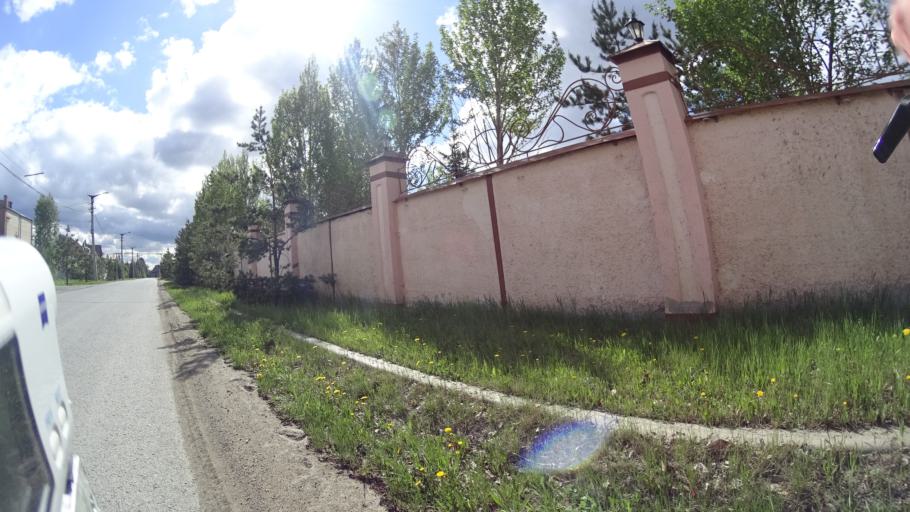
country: RU
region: Chelyabinsk
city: Sargazy
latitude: 55.1458
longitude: 61.2345
